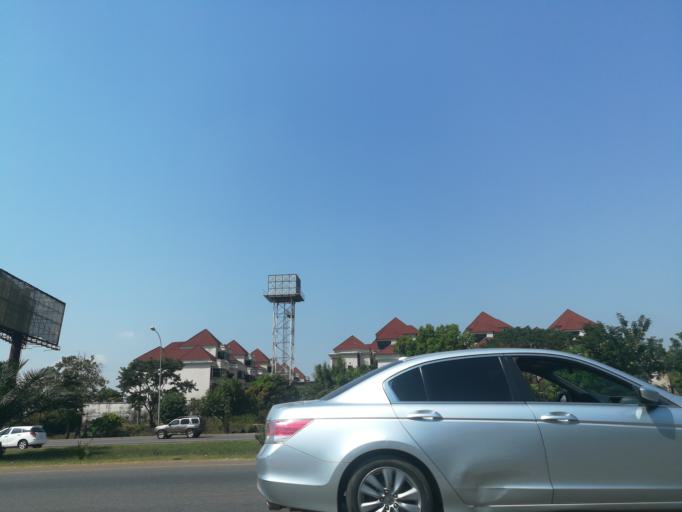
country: NG
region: Abuja Federal Capital Territory
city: Abuja
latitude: 9.0586
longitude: 7.4538
